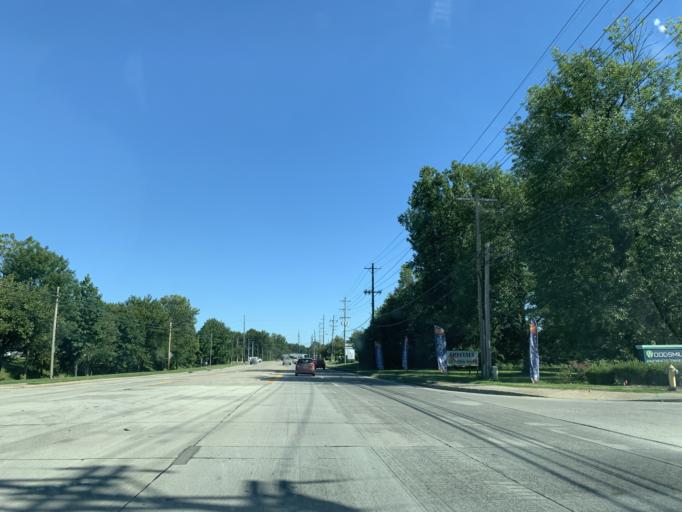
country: US
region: Kentucky
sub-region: Jefferson County
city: West Buechel
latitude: 38.1803
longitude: -85.6941
